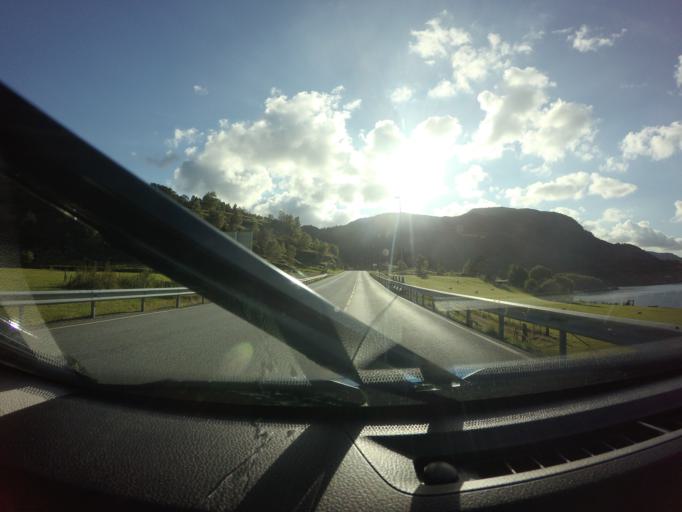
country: NO
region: Rogaland
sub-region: Forsand
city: Forsand
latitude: 58.8924
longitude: 6.0506
